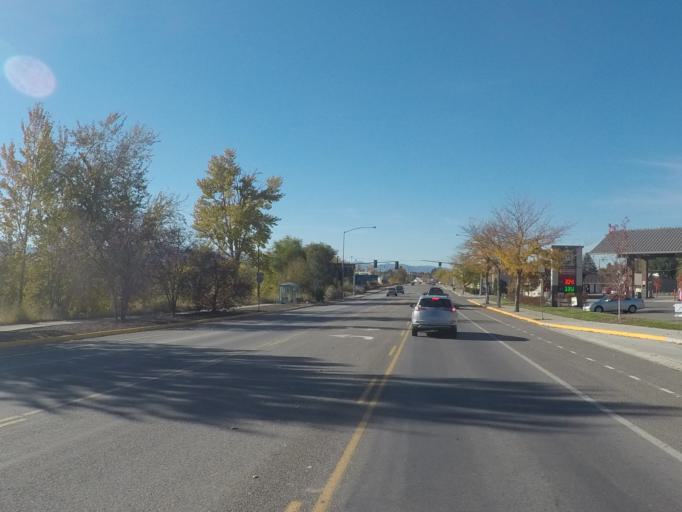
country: US
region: Montana
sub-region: Missoula County
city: Missoula
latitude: 46.8757
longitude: -114.0061
